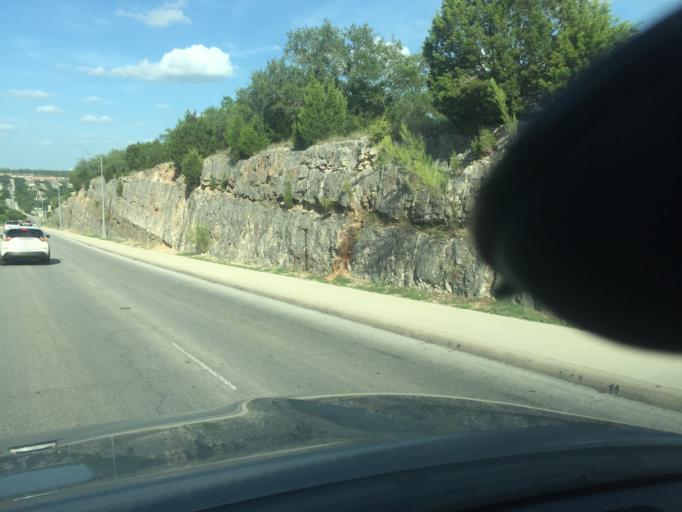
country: US
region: Texas
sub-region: Bexar County
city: Hollywood Park
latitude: 29.6424
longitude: -98.4868
